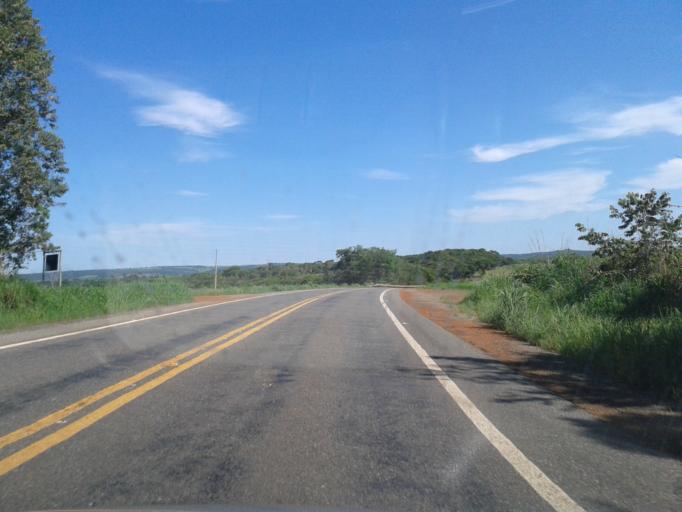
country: BR
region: Goias
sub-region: Piracanjuba
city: Piracanjuba
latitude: -17.3271
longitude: -48.8010
